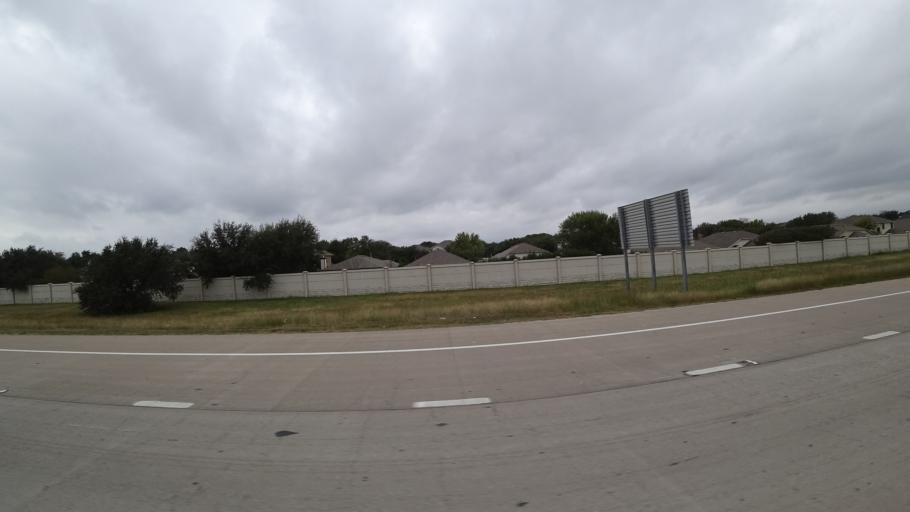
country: US
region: Texas
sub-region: Williamson County
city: Cedar Park
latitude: 30.5198
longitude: -97.8152
